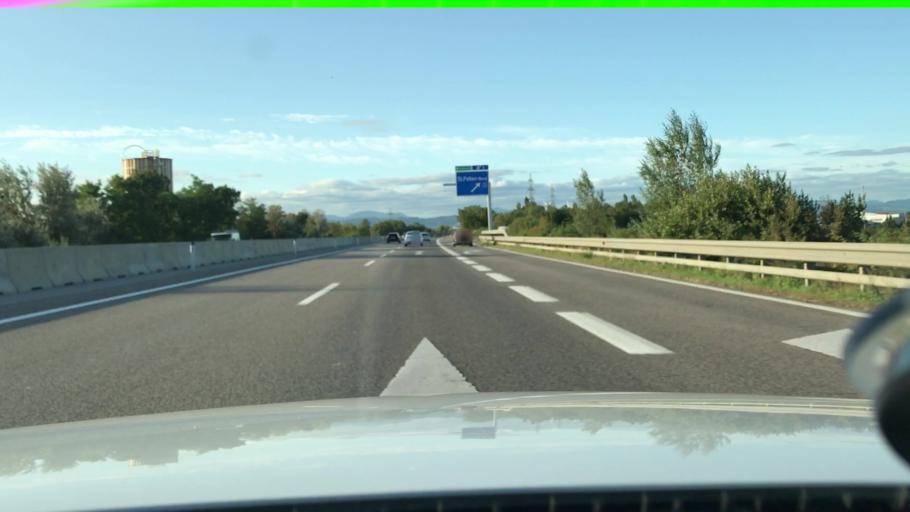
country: AT
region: Lower Austria
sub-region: Politischer Bezirk Sankt Polten
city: Herzogenburg
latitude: 48.2336
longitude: 15.6819
